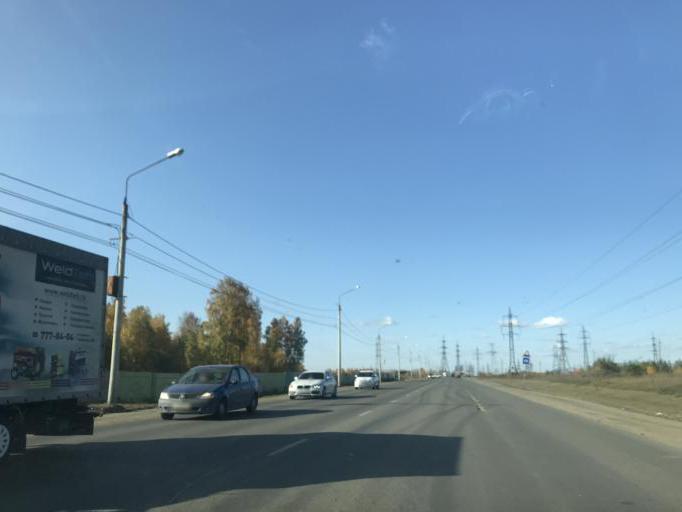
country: RU
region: Chelyabinsk
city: Roshchino
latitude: 55.2211
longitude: 61.2961
